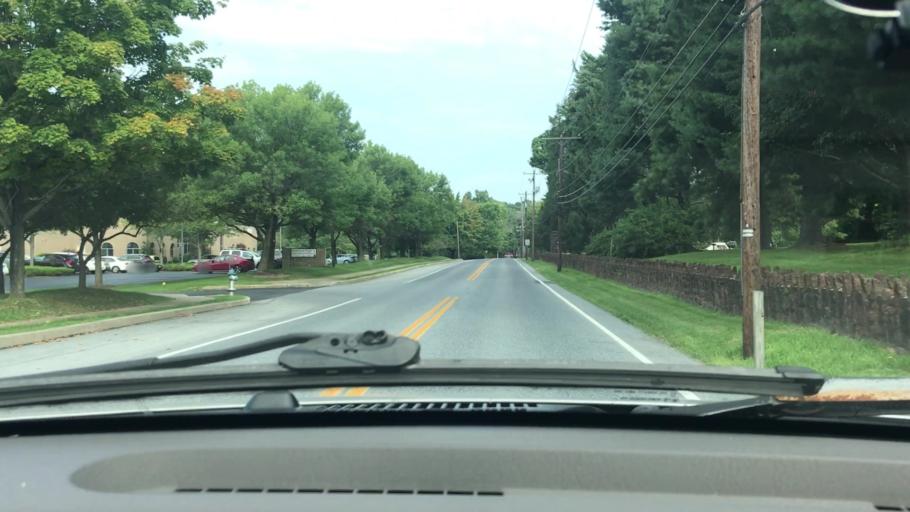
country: US
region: Pennsylvania
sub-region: Dauphin County
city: Middletown
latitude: 40.2059
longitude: -76.7598
